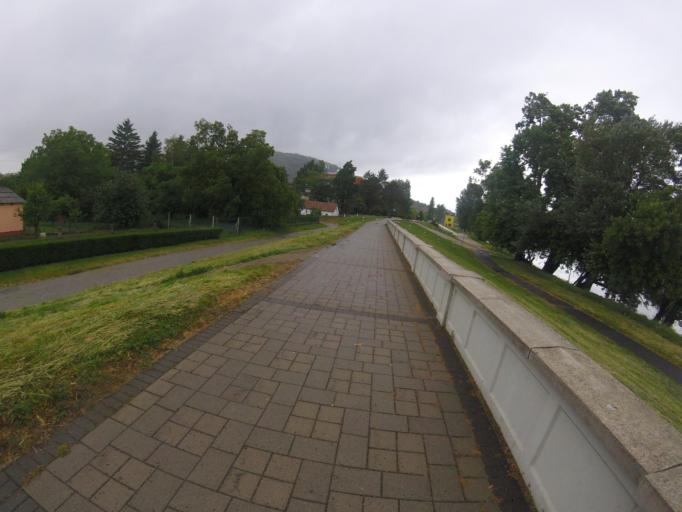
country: HU
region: Borsod-Abauj-Zemplen
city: Tokaj
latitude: 48.1131
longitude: 21.4161
